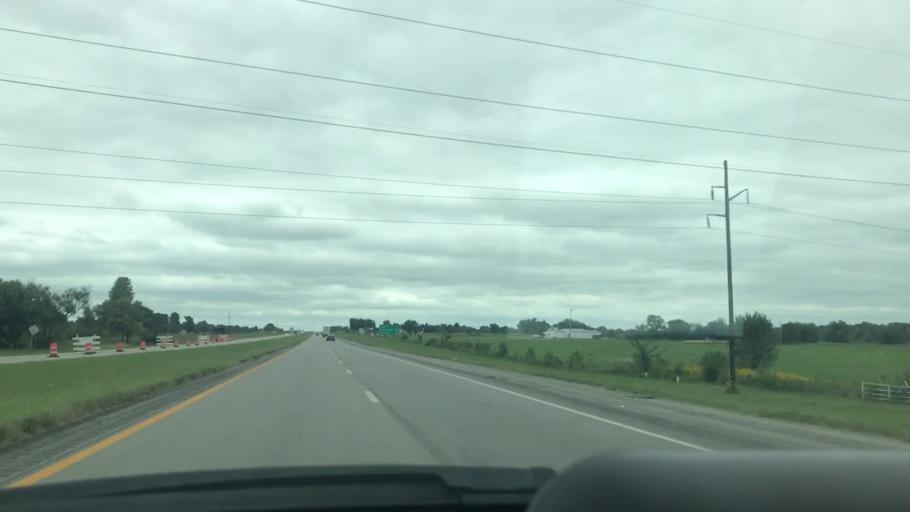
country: US
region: Oklahoma
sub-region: Mayes County
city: Pryor
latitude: 36.3216
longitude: -95.3136
